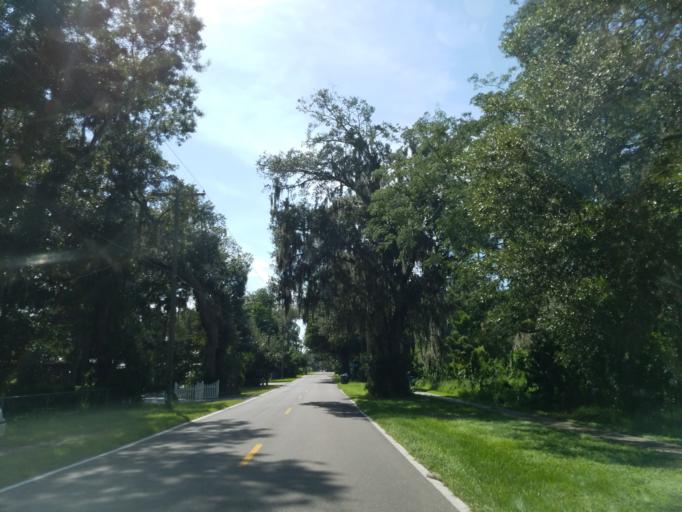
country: US
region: Florida
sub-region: Hillsborough County
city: Riverview
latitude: 27.8790
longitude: -82.3205
